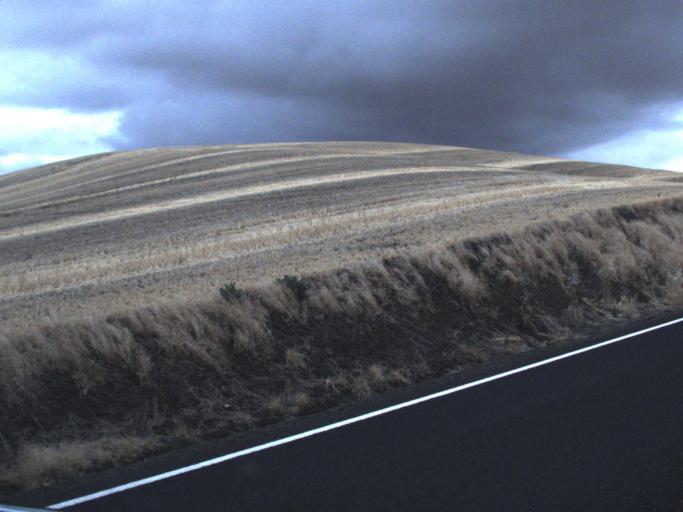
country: US
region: Washington
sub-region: Whitman County
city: Colfax
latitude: 47.1664
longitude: -117.2868
